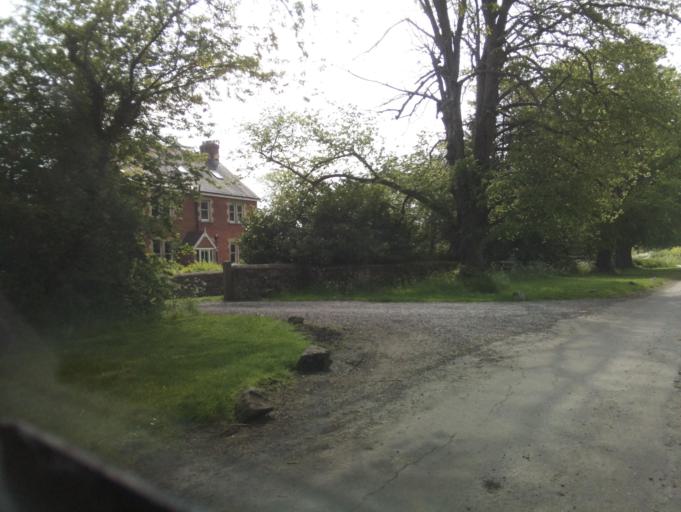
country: GB
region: England
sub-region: South Gloucestershire
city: Horton
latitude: 51.5423
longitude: -2.3598
